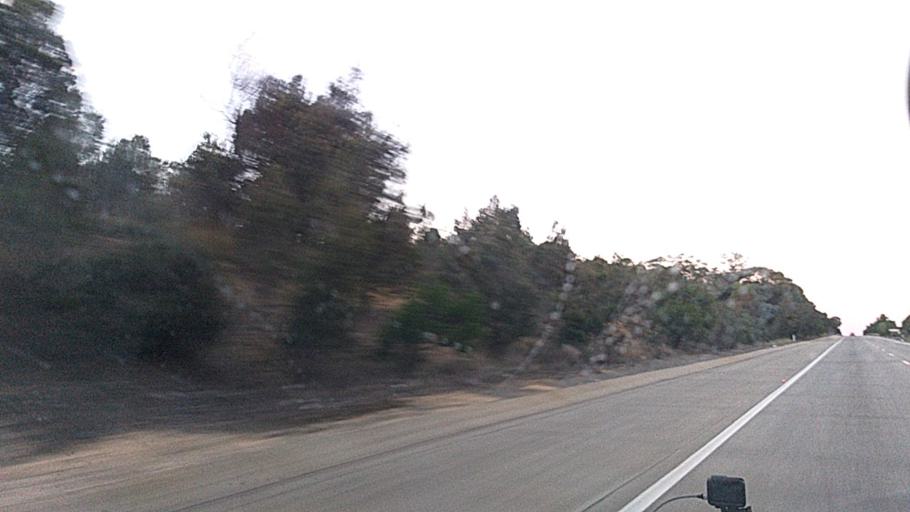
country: AU
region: New South Wales
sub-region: Wingecarribee
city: Bundanoon
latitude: -34.6761
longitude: 150.0606
